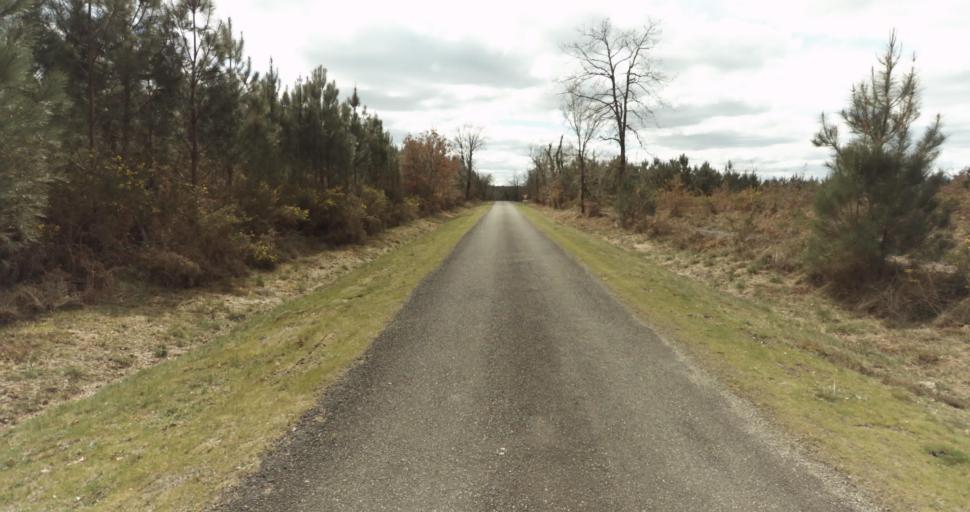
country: FR
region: Aquitaine
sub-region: Departement des Landes
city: Roquefort
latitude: 44.0633
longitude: -0.3991
